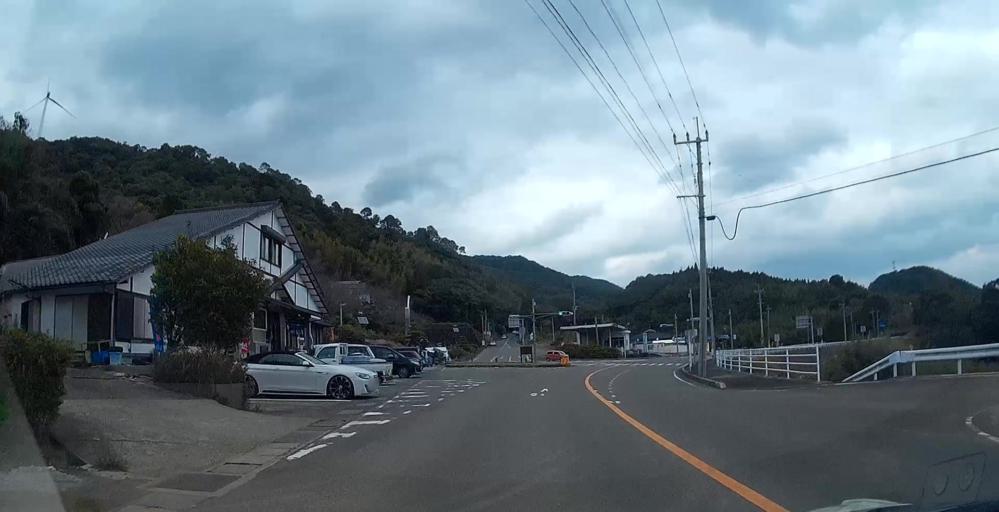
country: JP
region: Kagoshima
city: Akune
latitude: 32.1073
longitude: 130.1661
